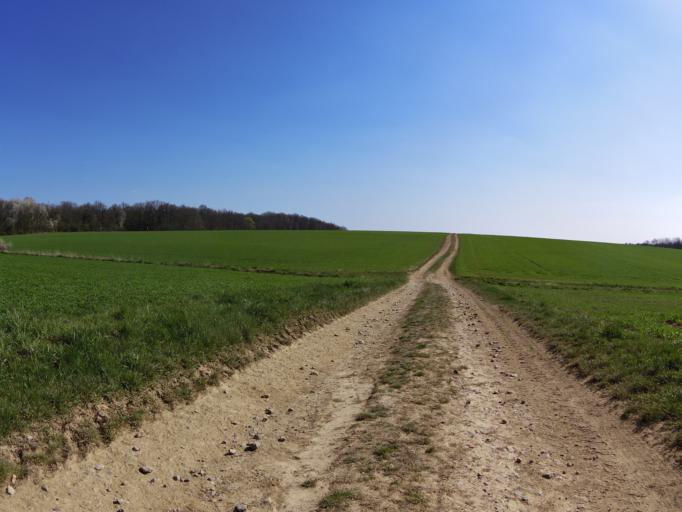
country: DE
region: Bavaria
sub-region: Regierungsbezirk Unterfranken
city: Kurnach
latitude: 49.8300
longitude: 10.0515
